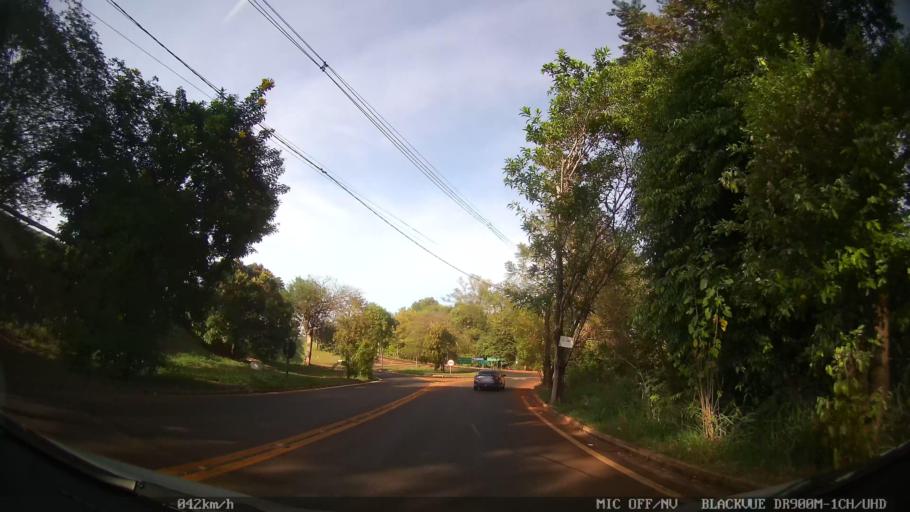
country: BR
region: Sao Paulo
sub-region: Ribeirao Preto
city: Ribeirao Preto
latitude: -21.2479
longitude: -47.8198
